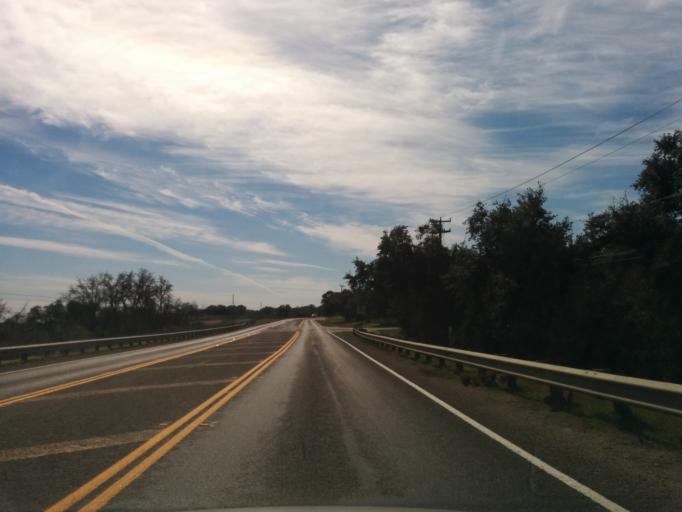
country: US
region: Texas
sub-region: Bexar County
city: Fair Oaks Ranch
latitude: 29.7211
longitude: -98.6237
